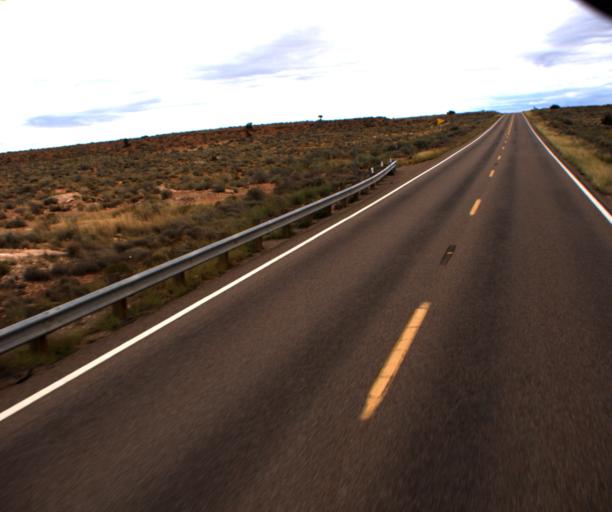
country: US
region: Arizona
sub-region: Navajo County
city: Holbrook
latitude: 34.7709
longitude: -110.1275
